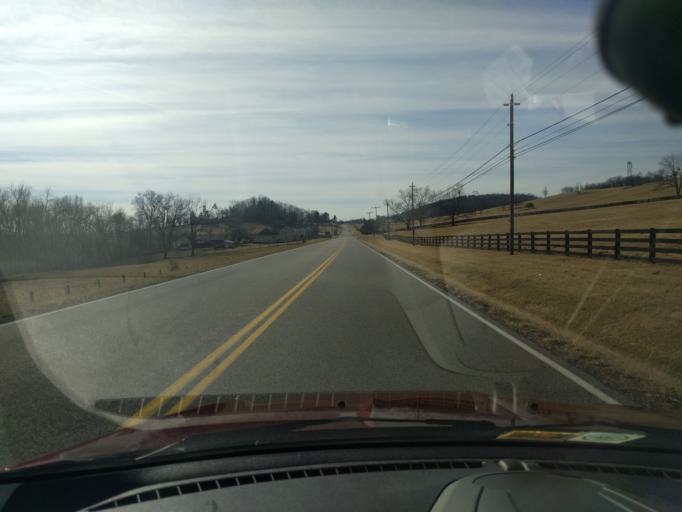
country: US
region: Virginia
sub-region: Augusta County
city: Weyers Cave
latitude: 38.2741
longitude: -78.9471
